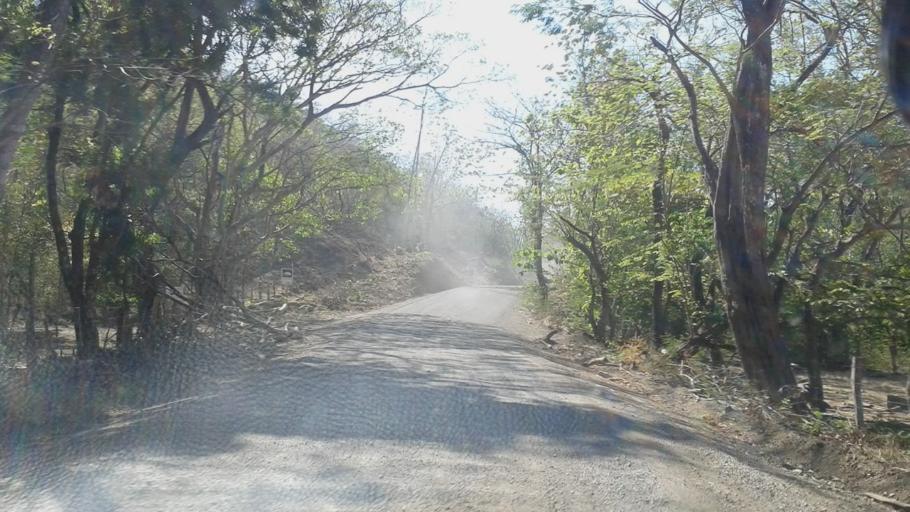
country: CR
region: Guanacaste
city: Santa Cruz
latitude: 10.1838
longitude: -85.7740
